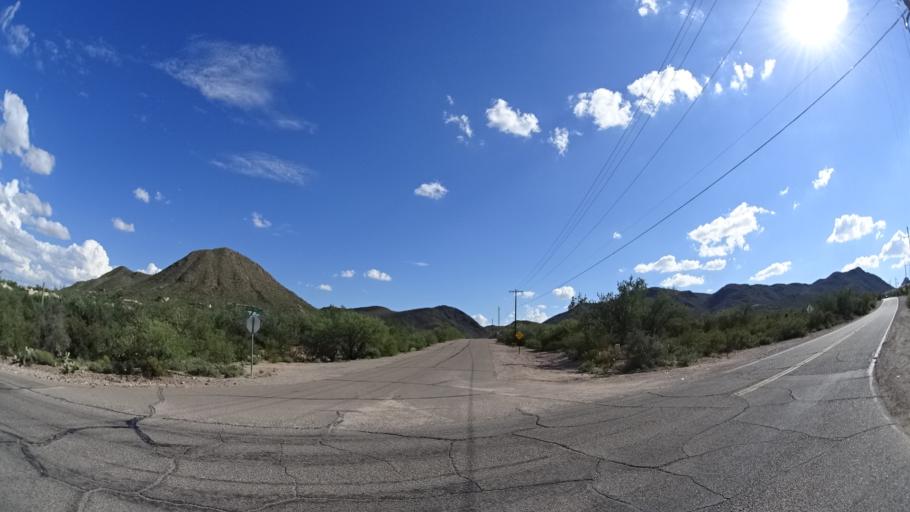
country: US
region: Arizona
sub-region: Pima County
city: Tucson Estates
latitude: 32.2357
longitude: -111.0628
